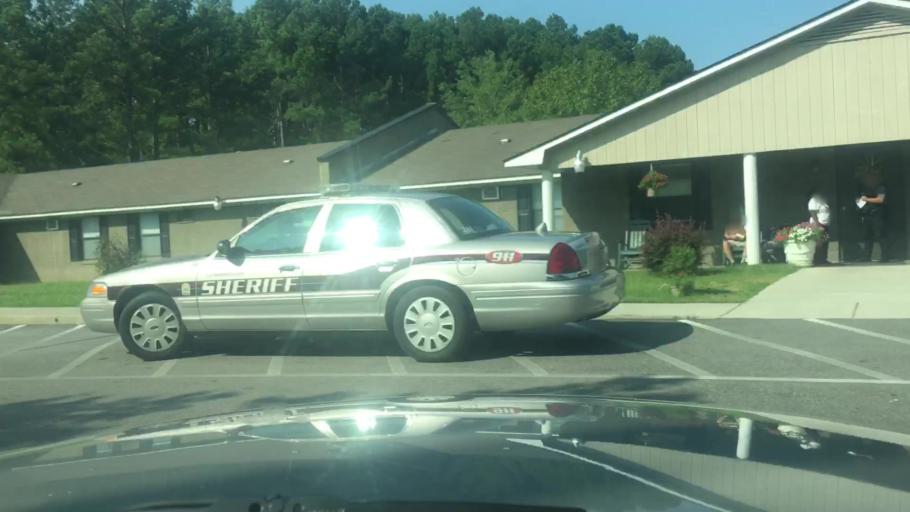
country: US
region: North Carolina
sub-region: Cumberland County
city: Fayetteville
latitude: 35.0248
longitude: -78.8431
